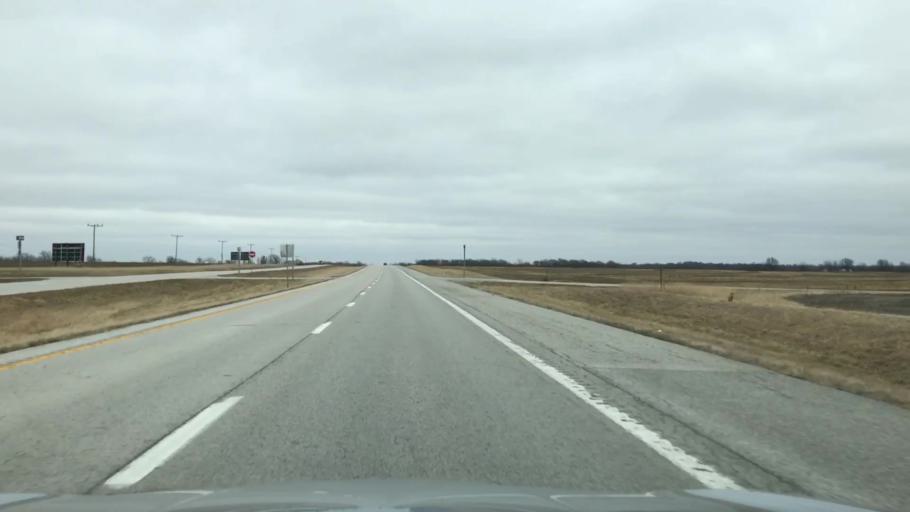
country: US
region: Missouri
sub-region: Livingston County
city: Chillicothe
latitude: 39.7763
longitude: -93.4640
